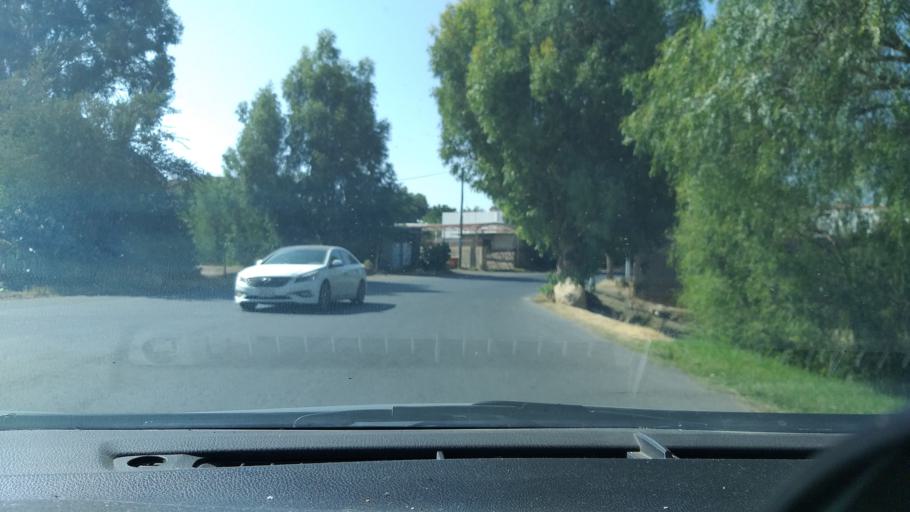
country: SA
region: Makkah
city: Ash Shafa
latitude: 21.0772
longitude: 40.3264
